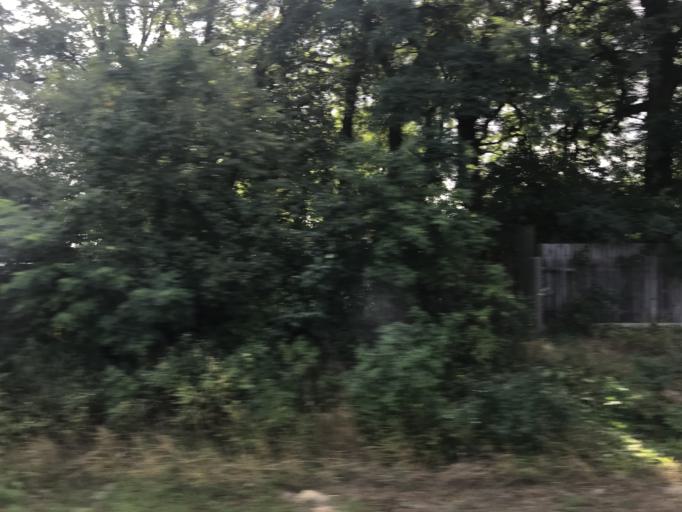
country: PL
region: Kujawsko-Pomorskie
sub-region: Powiat swiecki
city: Warlubie
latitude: 53.5925
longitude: 18.6256
